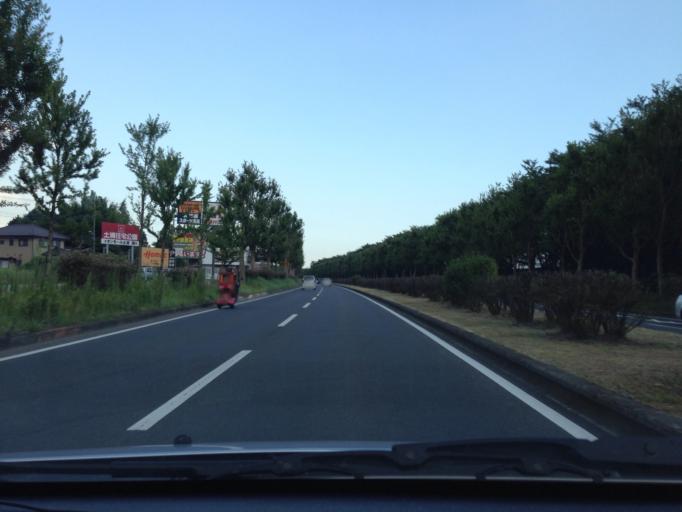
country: JP
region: Ibaraki
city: Naka
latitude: 36.0727
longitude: 140.1267
